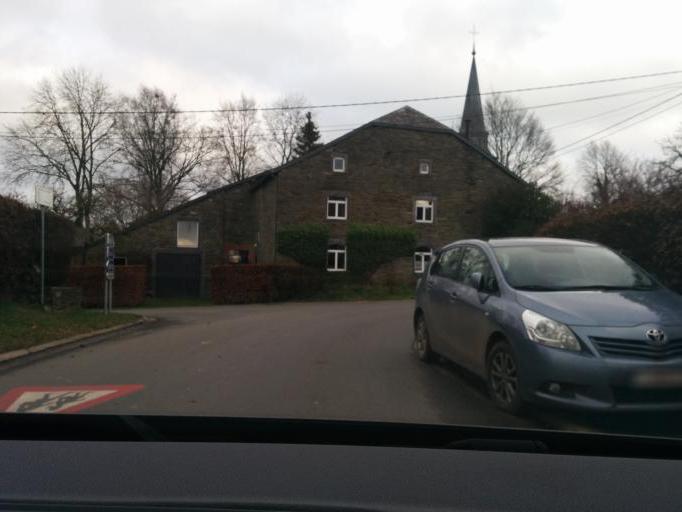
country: BE
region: Wallonia
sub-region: Province du Luxembourg
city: Gouvy
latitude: 50.1809
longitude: 5.8641
